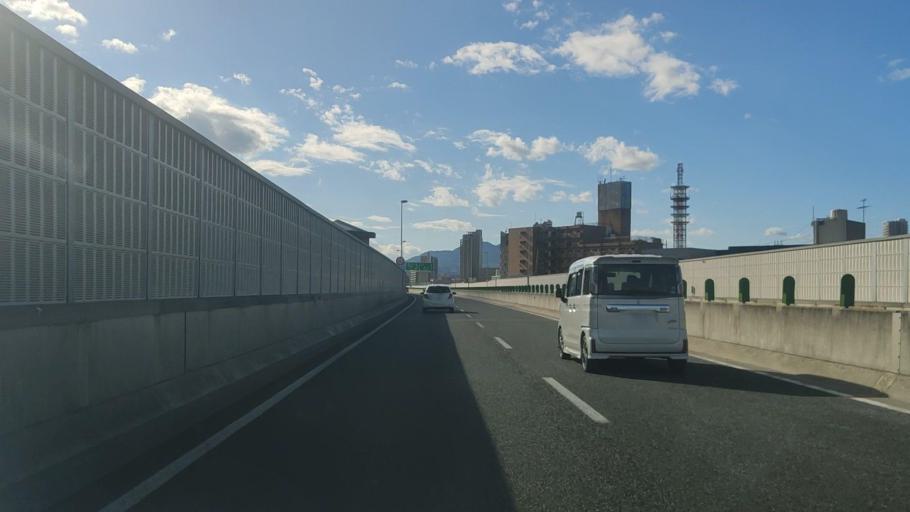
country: JP
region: Fukuoka
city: Kitakyushu
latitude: 33.8775
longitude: 130.8922
